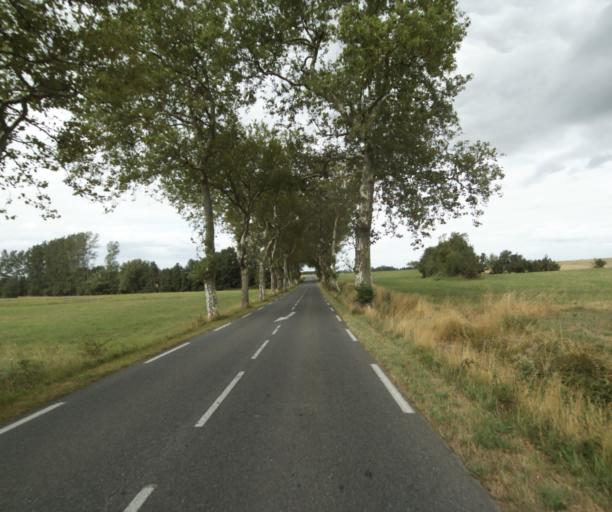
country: FR
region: Midi-Pyrenees
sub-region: Departement du Tarn
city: Soreze
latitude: 43.4604
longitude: 2.0788
